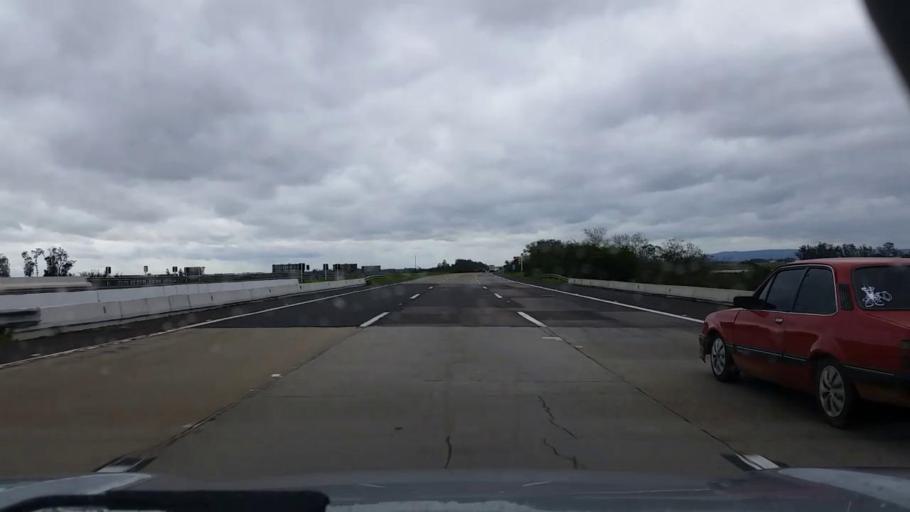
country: BR
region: Rio Grande do Sul
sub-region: Rolante
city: Rolante
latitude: -29.8863
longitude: -50.6359
